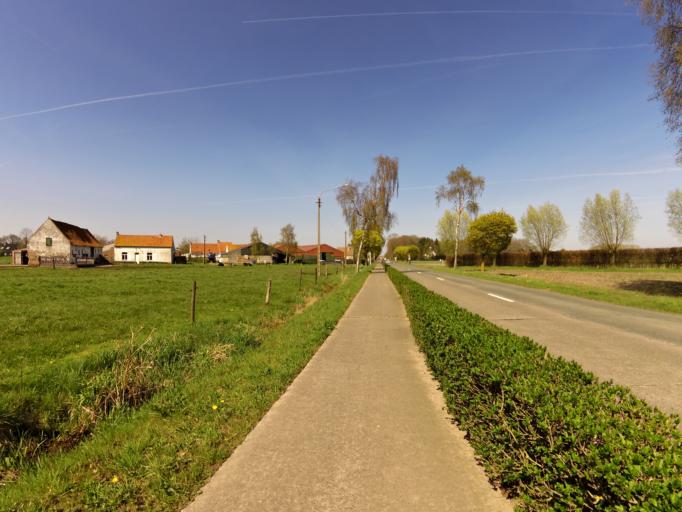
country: BE
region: Flanders
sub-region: Provincie West-Vlaanderen
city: Jabbeke
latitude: 51.1721
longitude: 3.0865
